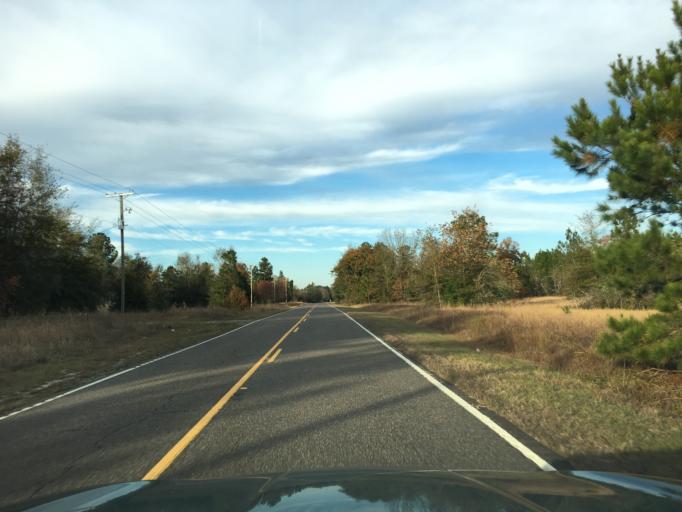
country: US
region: South Carolina
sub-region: Lexington County
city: Leesville
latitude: 33.6874
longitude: -81.3647
